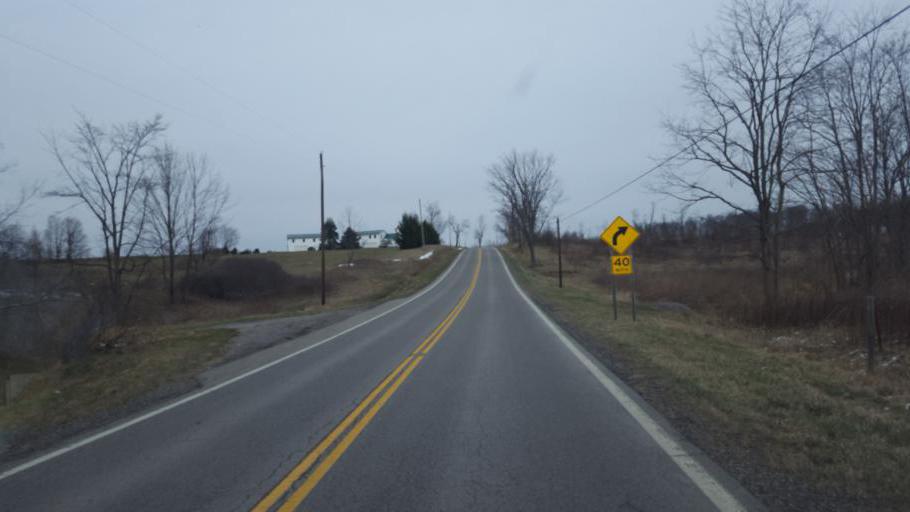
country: US
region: Ohio
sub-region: Richland County
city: Lexington
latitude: 40.6398
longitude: -82.5926
